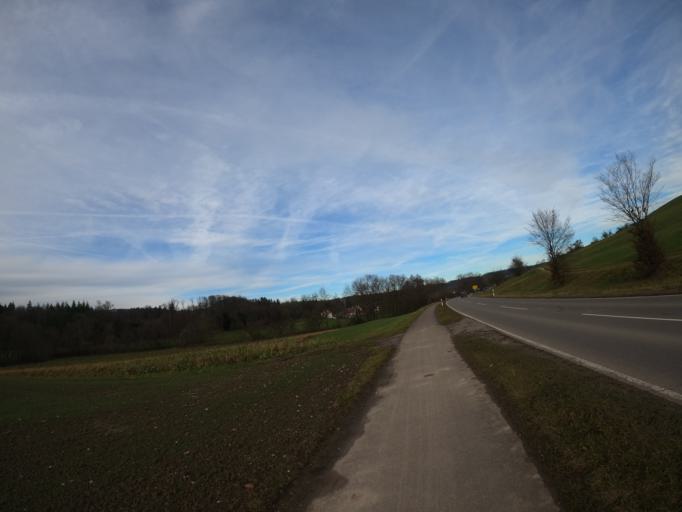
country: DE
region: Baden-Wuerttemberg
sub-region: Regierungsbezirk Stuttgart
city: Ottenbach
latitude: 48.7179
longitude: 9.7359
